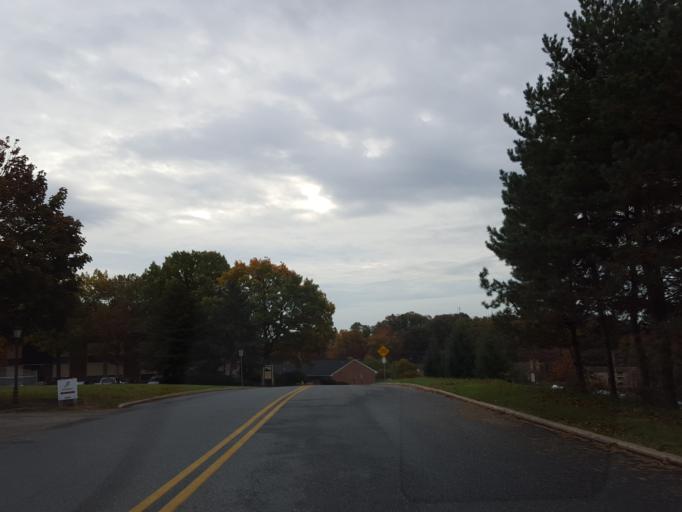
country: US
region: Pennsylvania
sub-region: York County
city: Valley View
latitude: 39.9434
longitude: -76.6927
